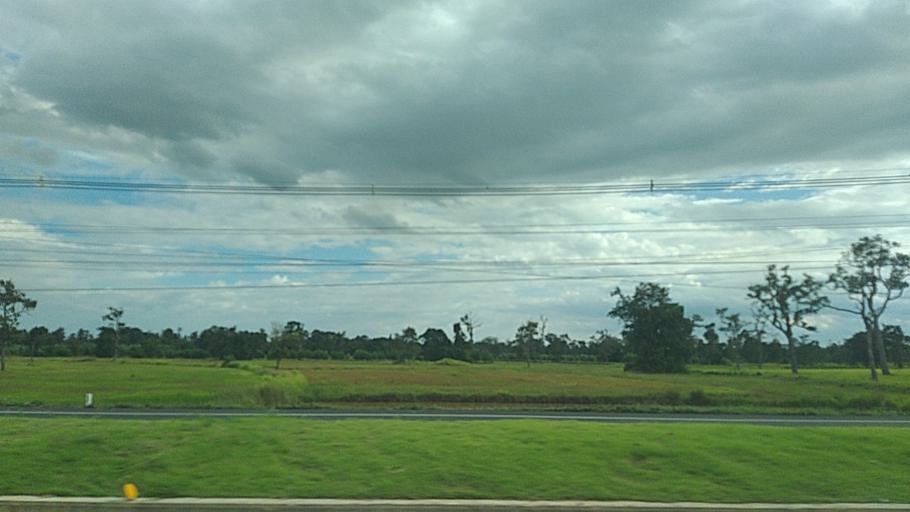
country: TH
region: Surin
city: Prasat
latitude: 14.5991
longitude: 103.4367
